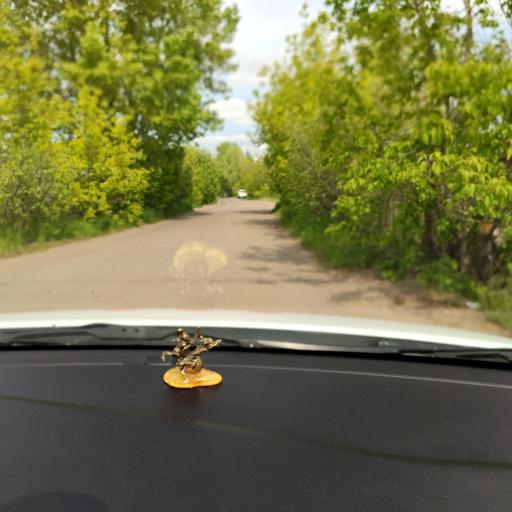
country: RU
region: Tatarstan
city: Verkhniy Uslon
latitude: 55.6984
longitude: 49.0604
